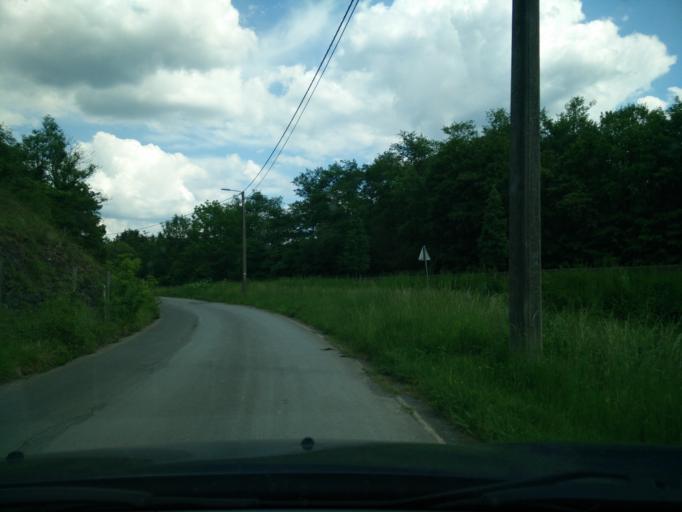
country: BE
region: Wallonia
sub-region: Province de Namur
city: Couvin
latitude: 50.0749
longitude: 4.6017
